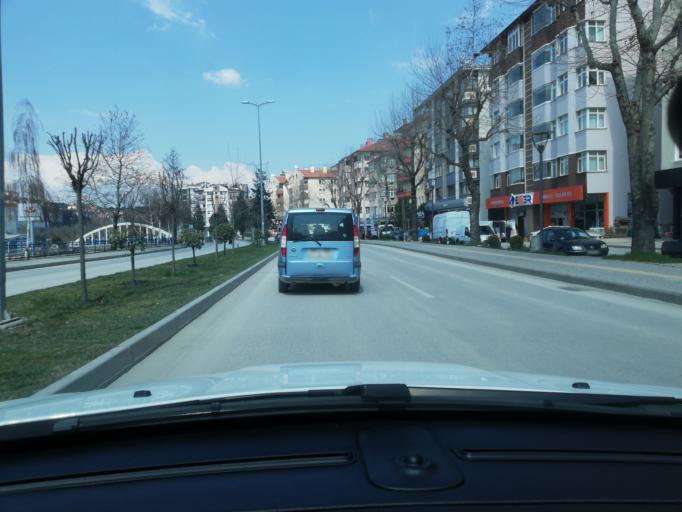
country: TR
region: Kastamonu
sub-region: Cide
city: Kastamonu
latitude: 41.3934
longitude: 33.7820
